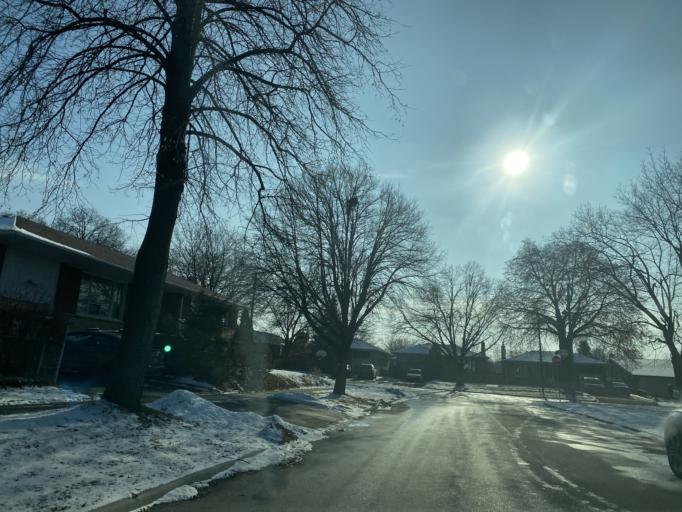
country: CA
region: Ontario
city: Etobicoke
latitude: 43.6726
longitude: -79.5671
